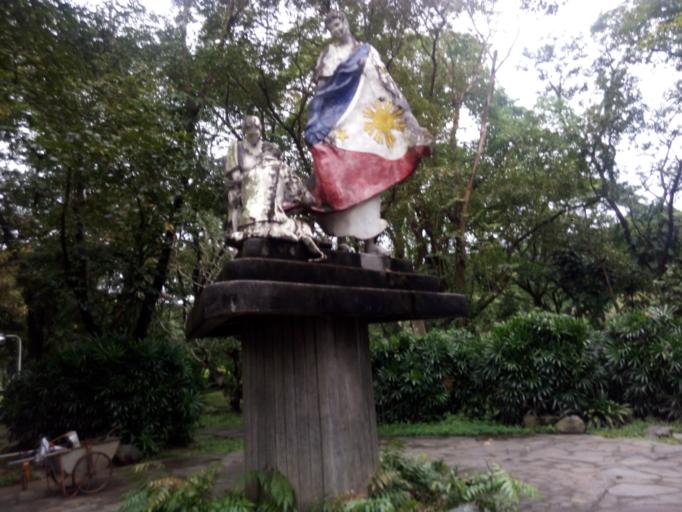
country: PH
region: Metro Manila
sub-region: Quezon City
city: Quezon City
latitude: 14.6550
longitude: 121.0663
